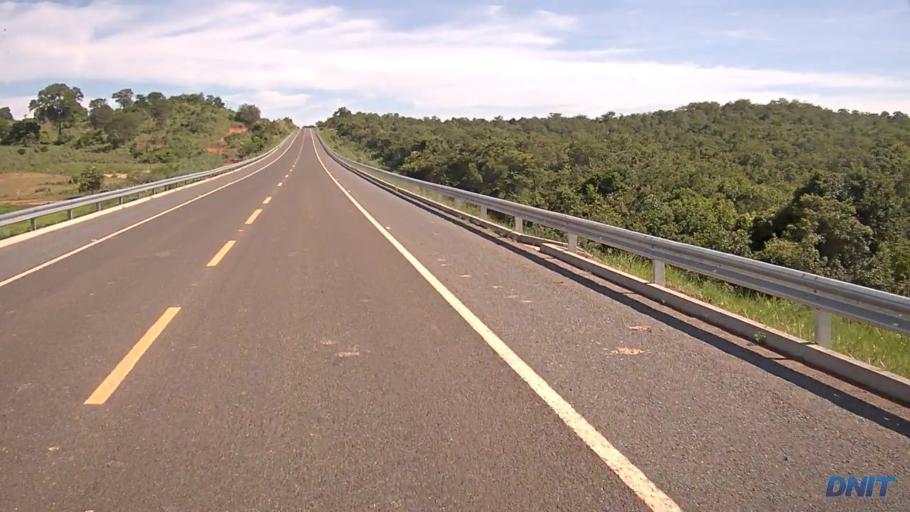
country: BR
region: Goias
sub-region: Sao Miguel Do Araguaia
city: Sao Miguel do Araguaia
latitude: -13.3343
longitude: -50.1540
